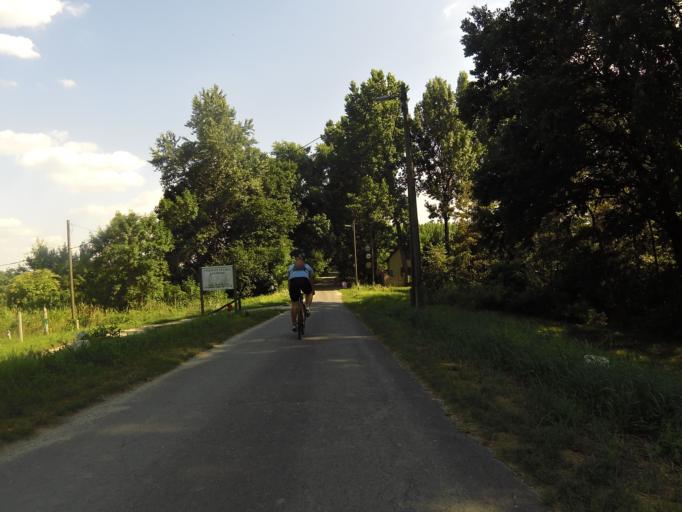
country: HU
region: Jasz-Nagykun-Szolnok
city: Abadszalok
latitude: 47.5373
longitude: 20.6327
